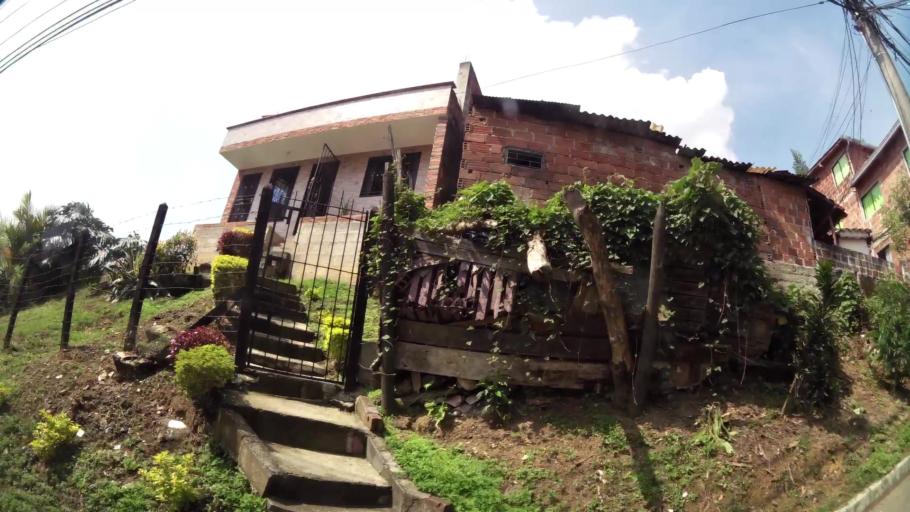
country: CO
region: Antioquia
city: La Estrella
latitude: 6.1788
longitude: -75.6385
